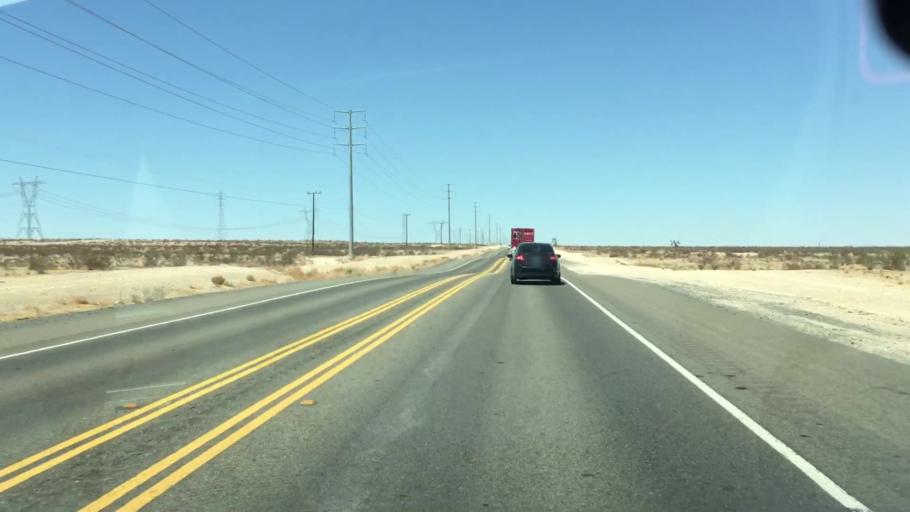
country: US
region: California
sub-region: San Bernardino County
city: Adelanto
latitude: 34.6629
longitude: -117.4407
